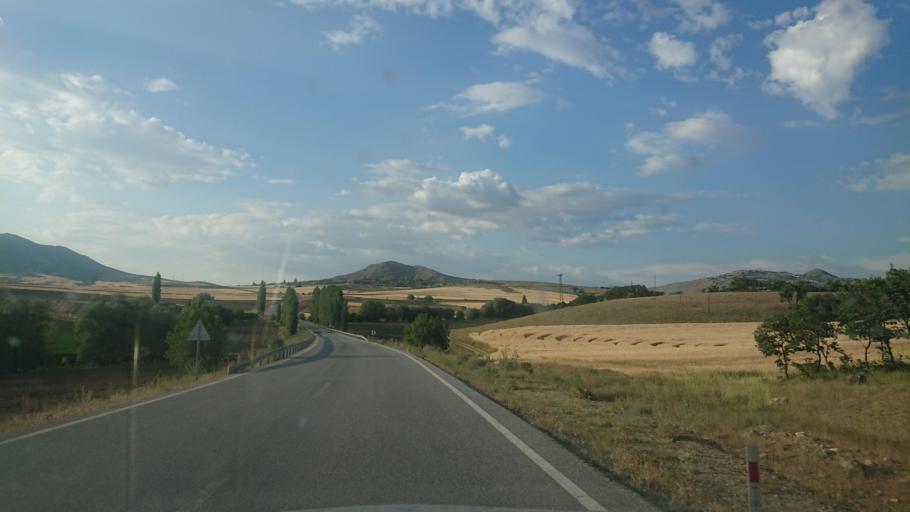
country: TR
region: Aksaray
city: Balci
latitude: 38.5701
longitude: 34.1057
